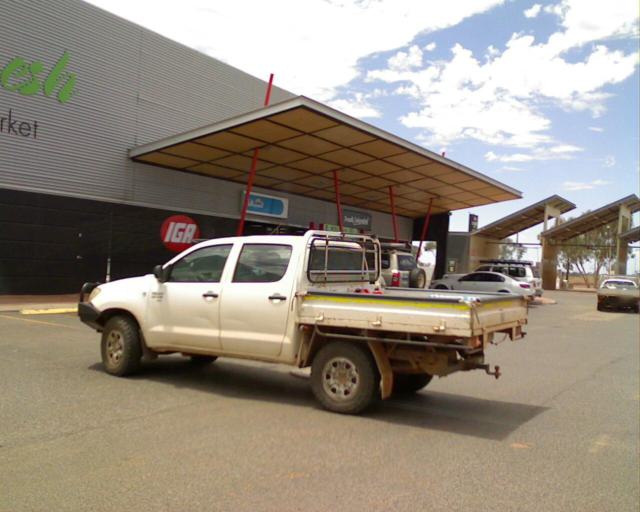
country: AU
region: Western Australia
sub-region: Kalgoorlie/Boulder
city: Boulder
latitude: -30.7754
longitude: 121.4605
